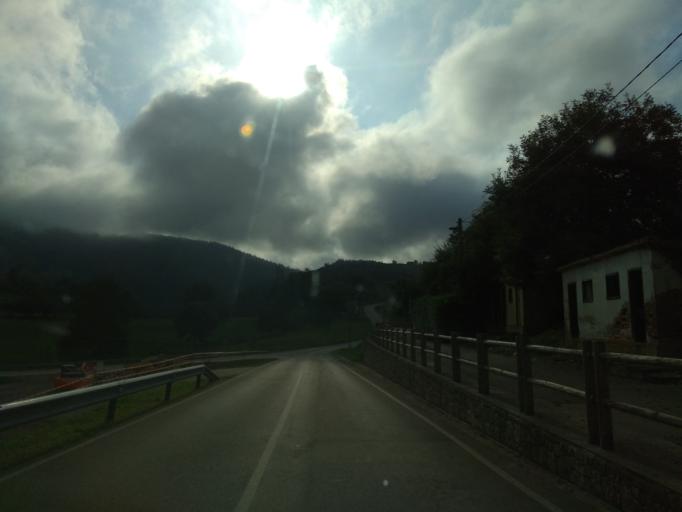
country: ES
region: Cantabria
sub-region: Provincia de Cantabria
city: San Vicente de la Barquera
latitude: 43.3102
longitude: -4.3908
